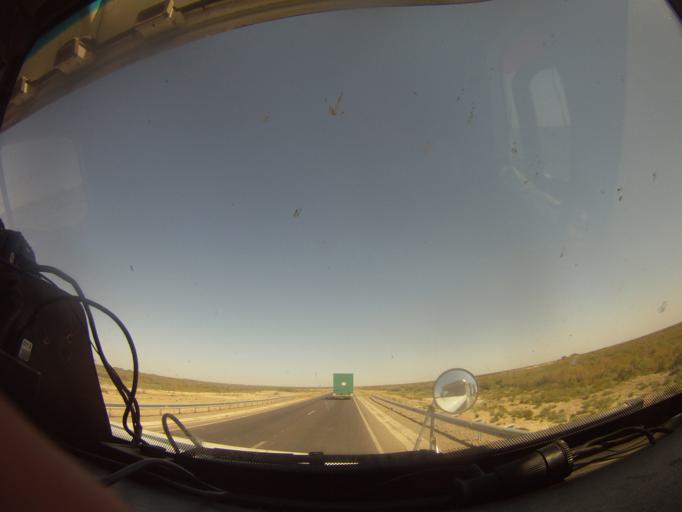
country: KZ
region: Qyzylorda
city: Terenozek
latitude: 44.8845
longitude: 65.1583
